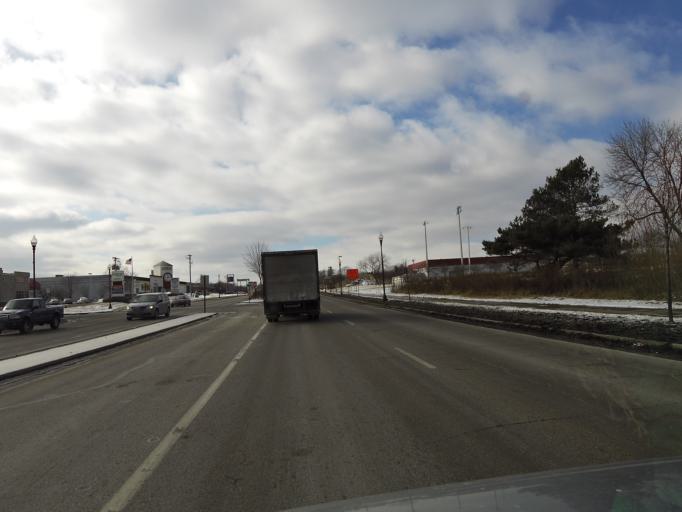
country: US
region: Minnesota
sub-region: Hennepin County
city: Minnetonka Mills
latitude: 44.9209
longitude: -93.4172
